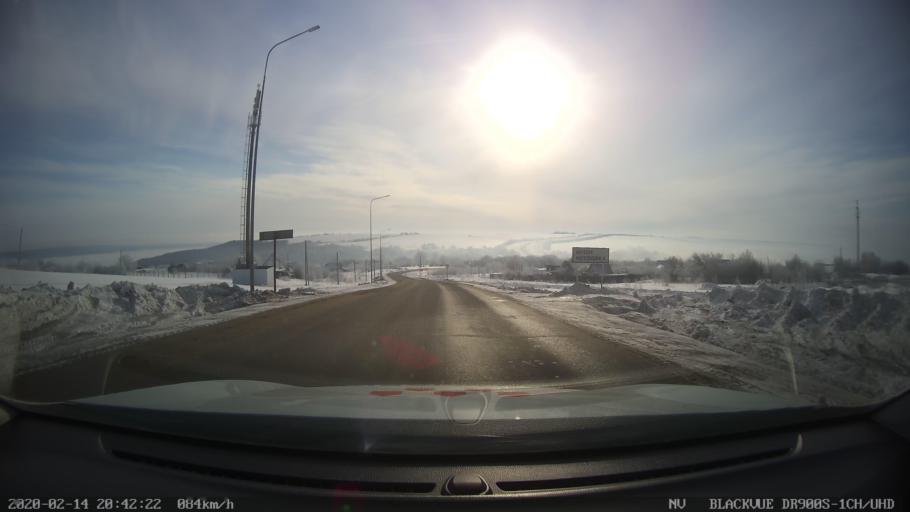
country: RU
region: Tatarstan
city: Kuybyshevskiy Zaton
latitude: 55.3177
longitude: 49.1415
